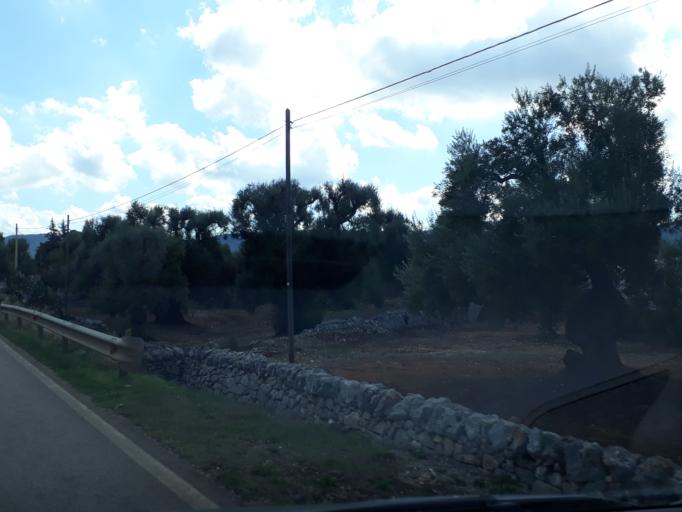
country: IT
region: Apulia
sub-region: Provincia di Brindisi
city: Pezze di Greco
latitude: 40.8109
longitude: 17.3852
